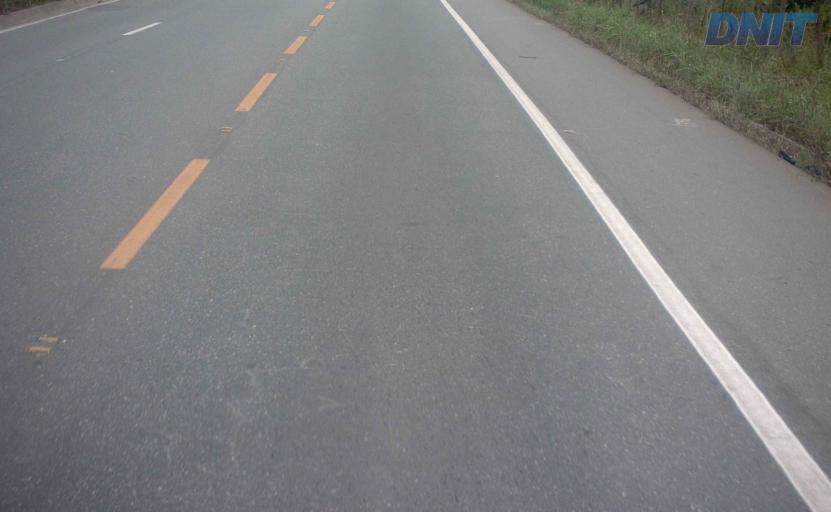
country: BR
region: Minas Gerais
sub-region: Nova Era
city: Nova Era
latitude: -19.7146
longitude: -43.0009
